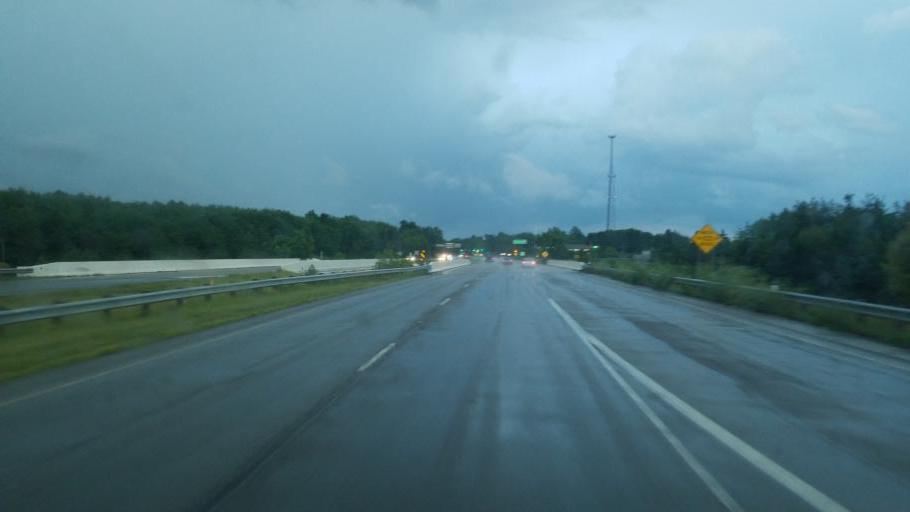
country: US
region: Ohio
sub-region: Wayne County
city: Doylestown
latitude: 40.9939
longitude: -81.6628
